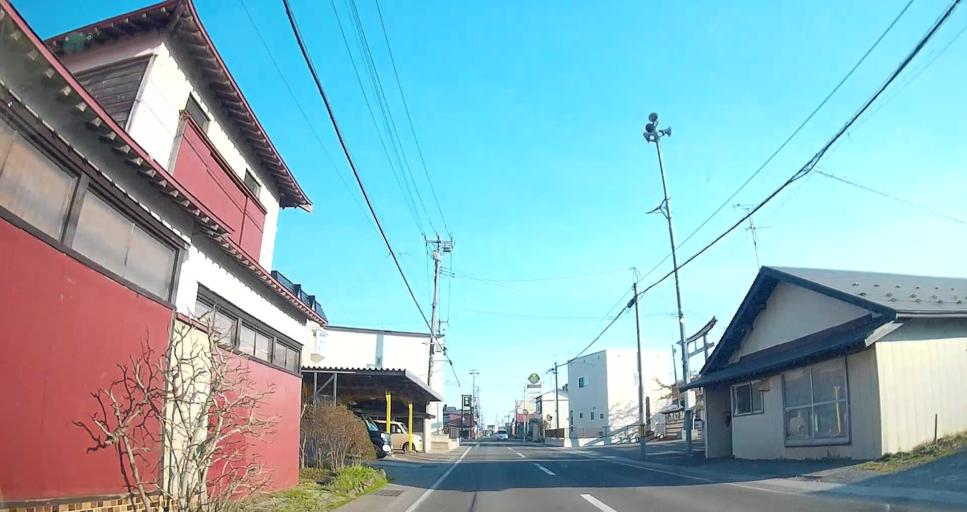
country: JP
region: Aomori
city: Mutsu
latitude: 41.2896
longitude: 141.2110
